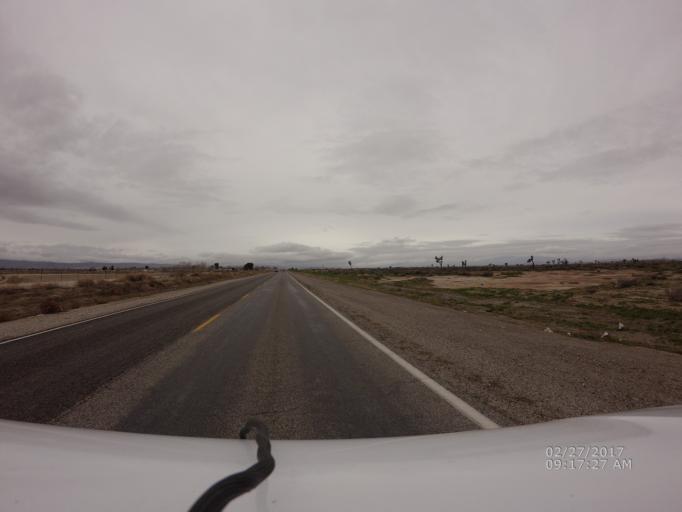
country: US
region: California
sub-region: Los Angeles County
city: Lancaster
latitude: 34.7189
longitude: -118.1019
